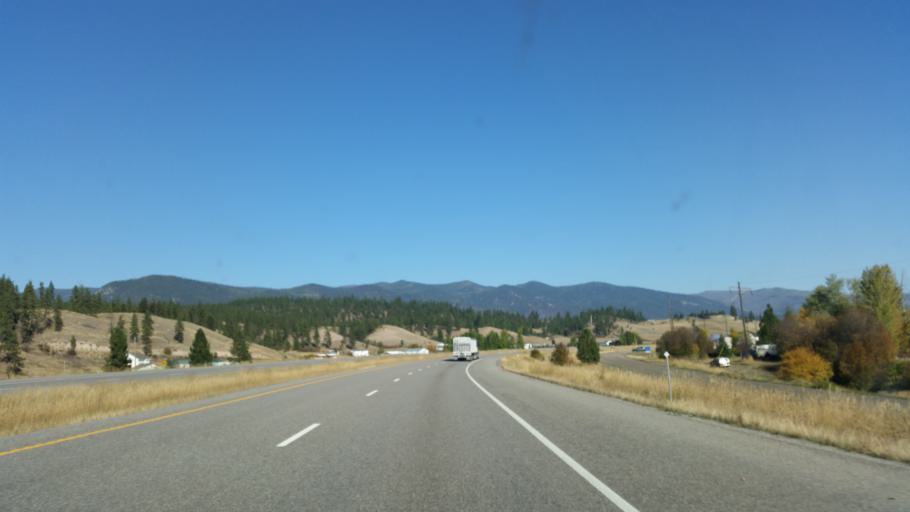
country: US
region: Montana
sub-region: Missoula County
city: Frenchtown
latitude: 47.0336
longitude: -114.3468
